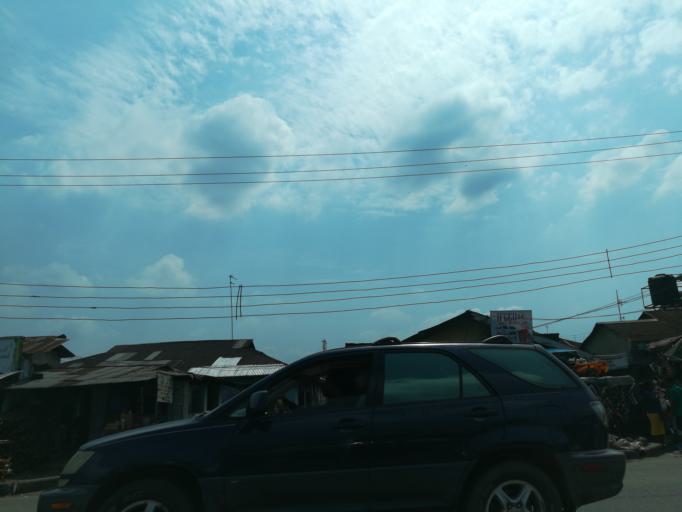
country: NG
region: Rivers
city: Port Harcourt
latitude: 4.8300
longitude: 6.9819
